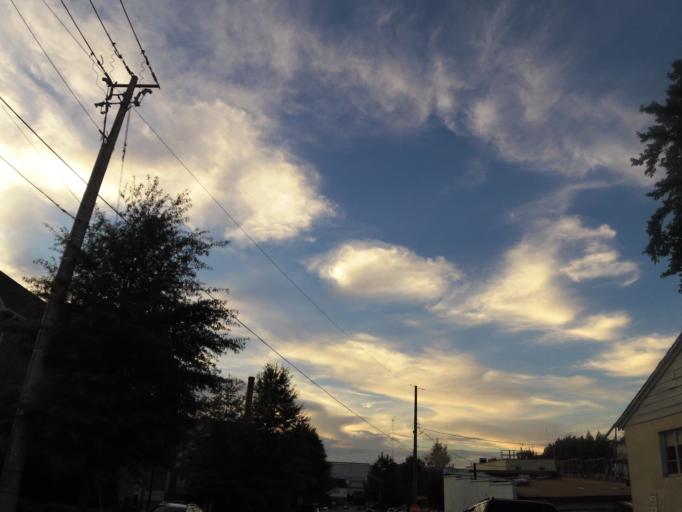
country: US
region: Tennessee
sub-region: Knox County
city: Knoxville
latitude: 35.9579
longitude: -83.9411
